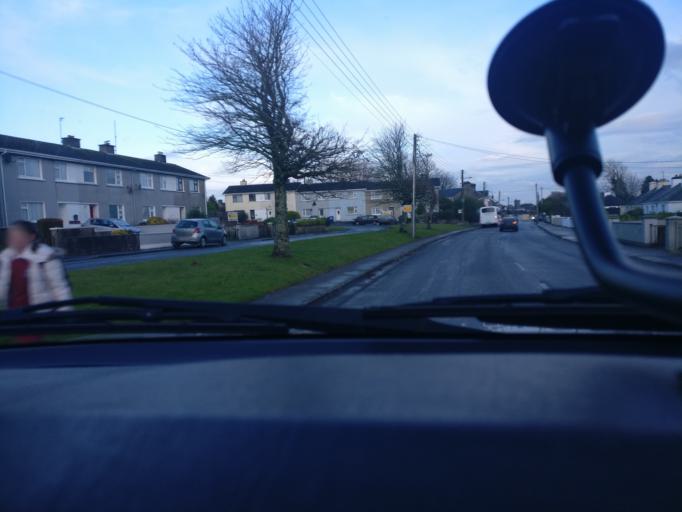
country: IE
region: Connaught
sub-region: County Galway
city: Loughrea
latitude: 53.1990
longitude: -8.5805
